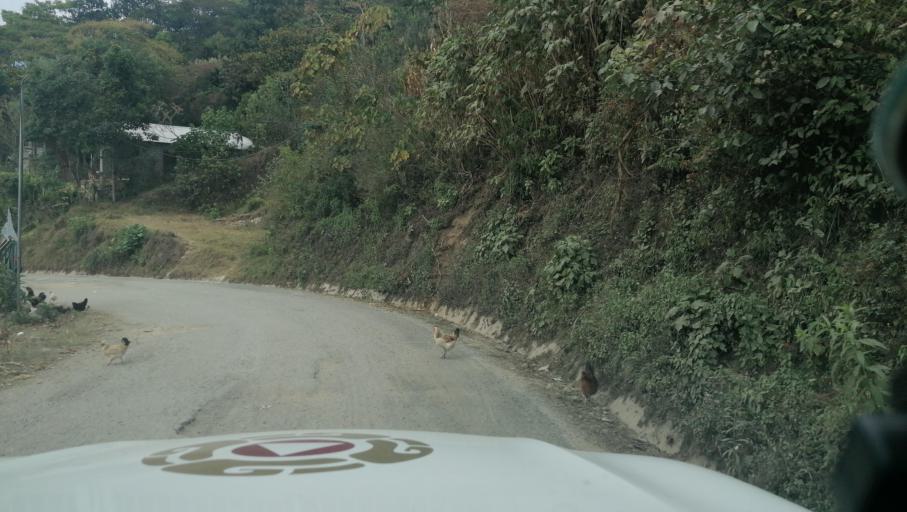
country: GT
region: San Marcos
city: Tacana
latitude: 15.2046
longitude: -92.1880
